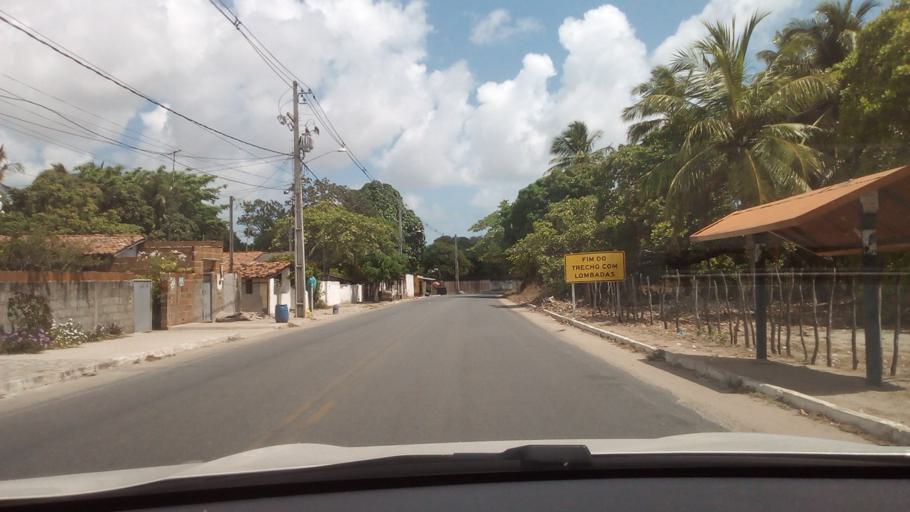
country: BR
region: Paraiba
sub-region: Conde
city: Conde
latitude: -7.2088
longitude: -34.8283
